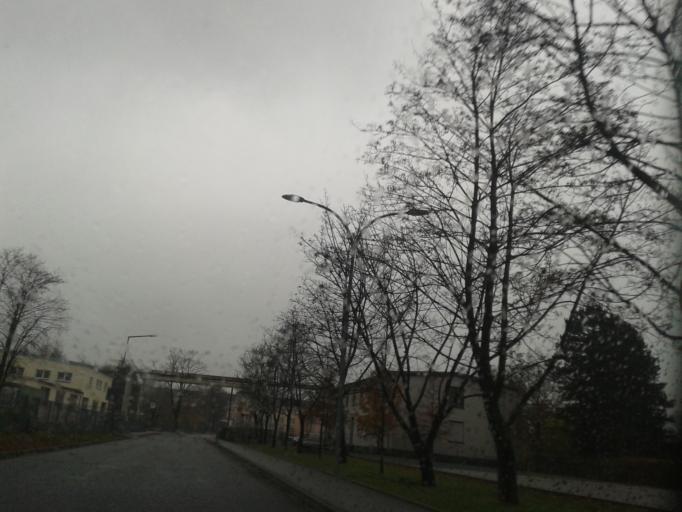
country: DE
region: Saxony
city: Heidenau
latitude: 51.0044
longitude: 13.8297
